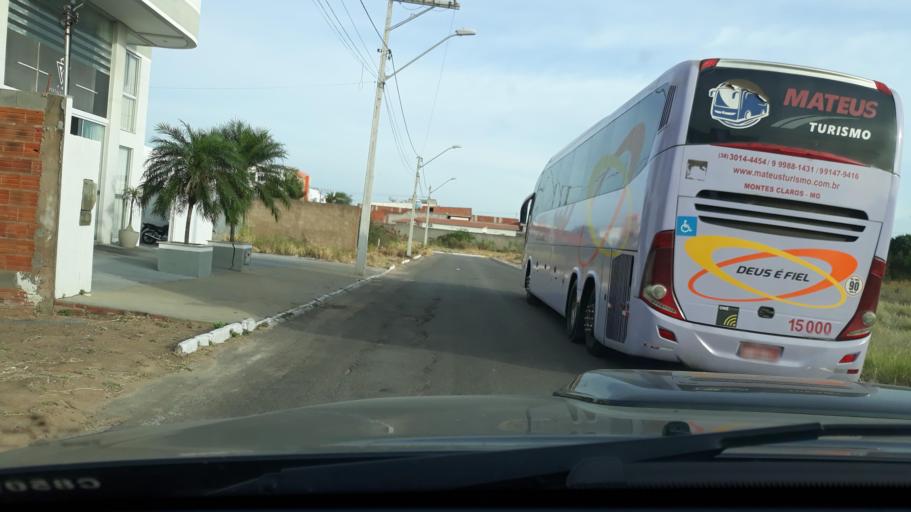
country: BR
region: Bahia
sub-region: Guanambi
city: Guanambi
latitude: -14.2111
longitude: -42.7679
